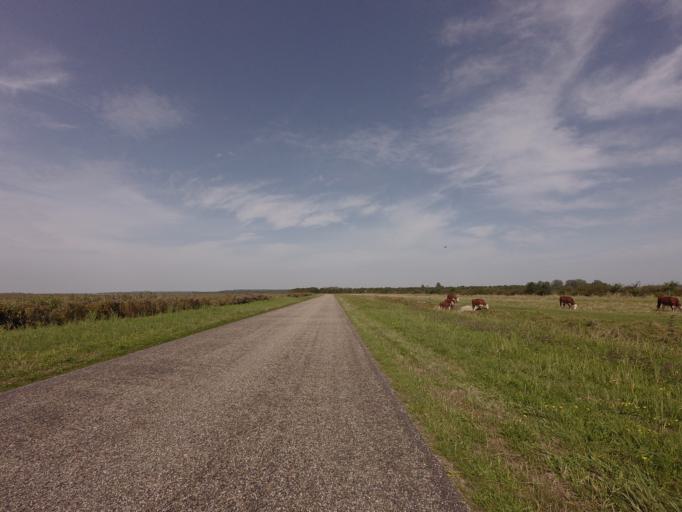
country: NL
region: Groningen
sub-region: Gemeente De Marne
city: Ulrum
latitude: 53.3528
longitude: 6.2654
